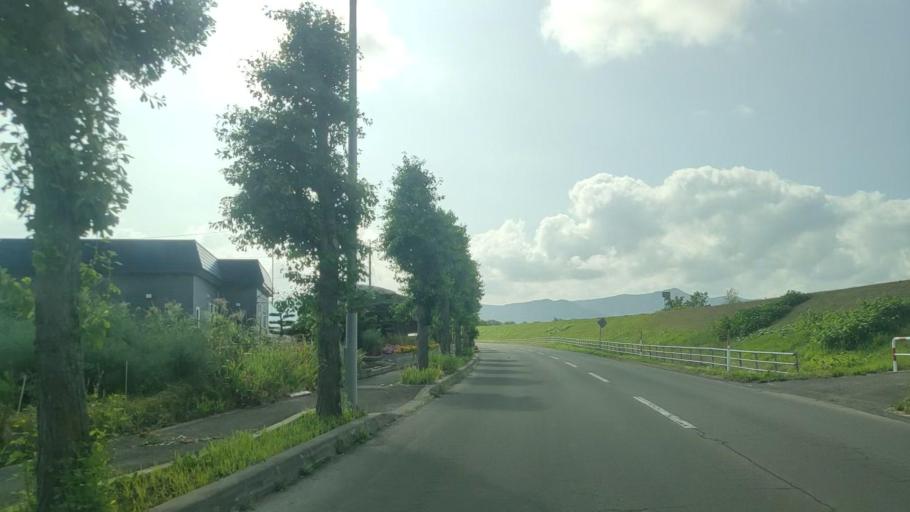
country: JP
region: Hokkaido
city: Shimo-furano
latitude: 43.3411
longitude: 142.3792
